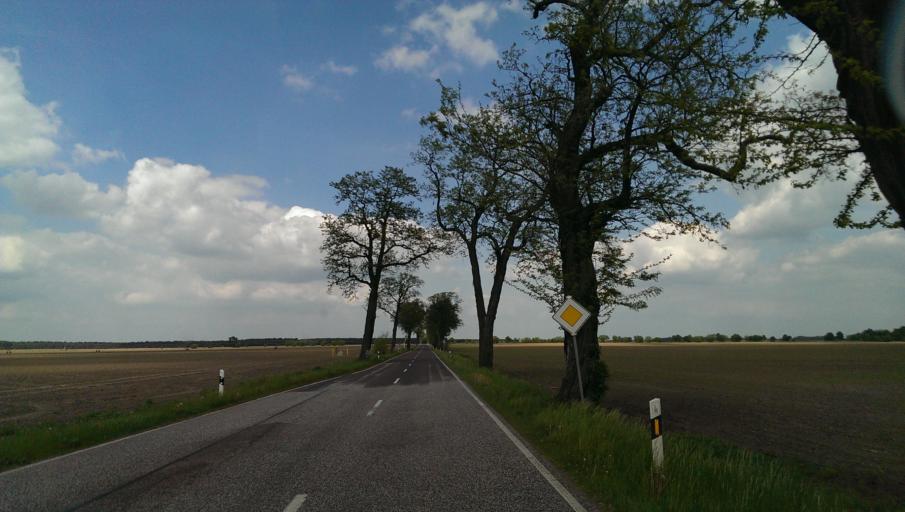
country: DE
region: Saxony-Anhalt
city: Tucheim
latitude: 52.1909
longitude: 12.1504
